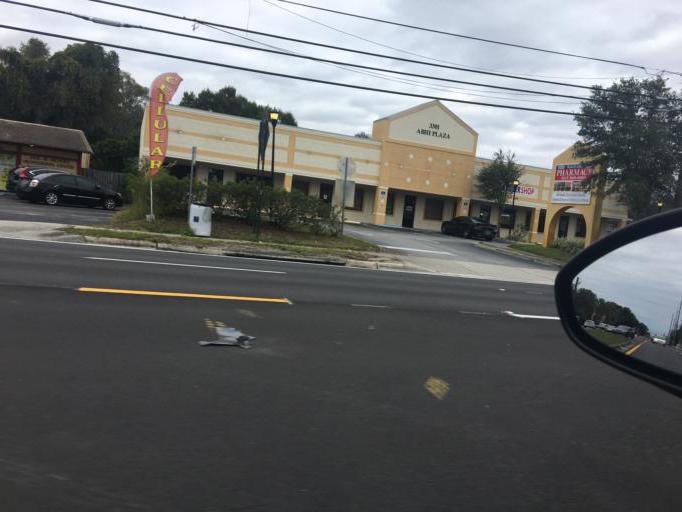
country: US
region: Florida
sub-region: Hillsborough County
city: Egypt Lake-Leto
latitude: 28.0254
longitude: -82.4950
